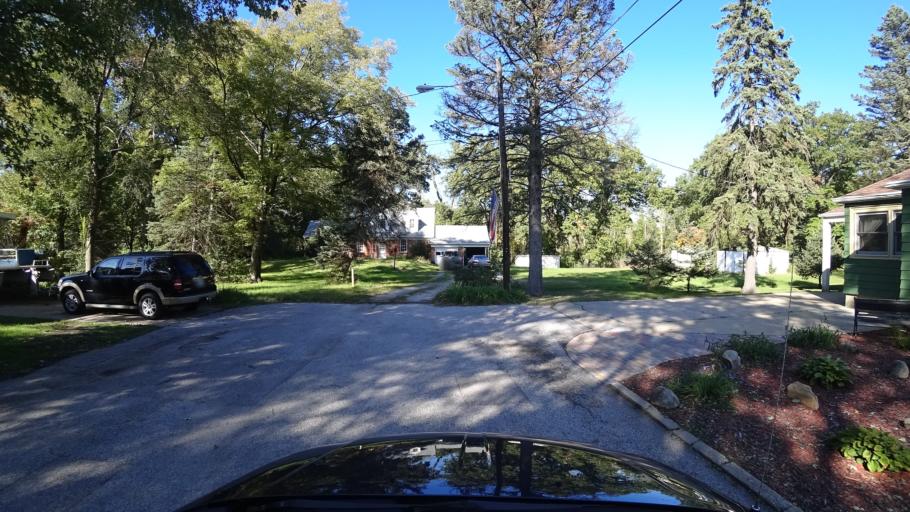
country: US
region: Indiana
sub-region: LaPorte County
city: Trail Creek
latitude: 41.7088
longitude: -86.8631
